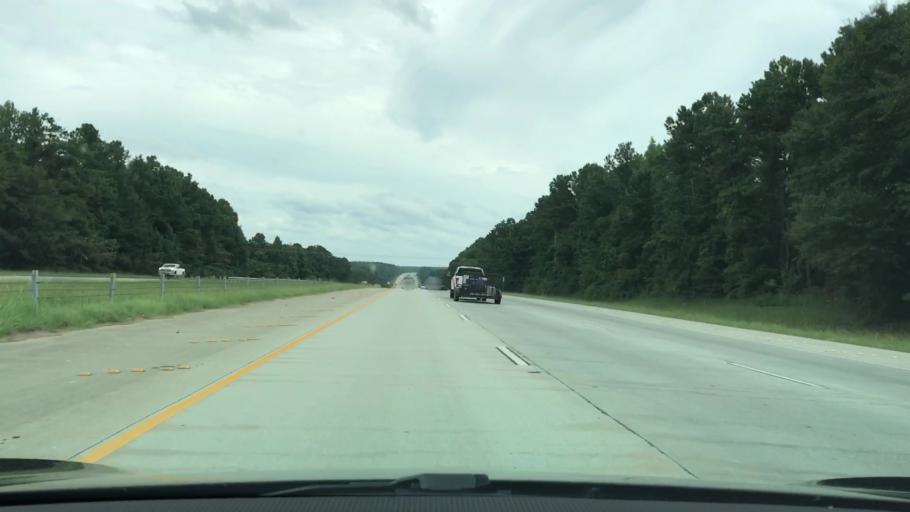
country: US
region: Georgia
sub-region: Coweta County
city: Grantville
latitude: 33.2802
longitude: -84.7998
